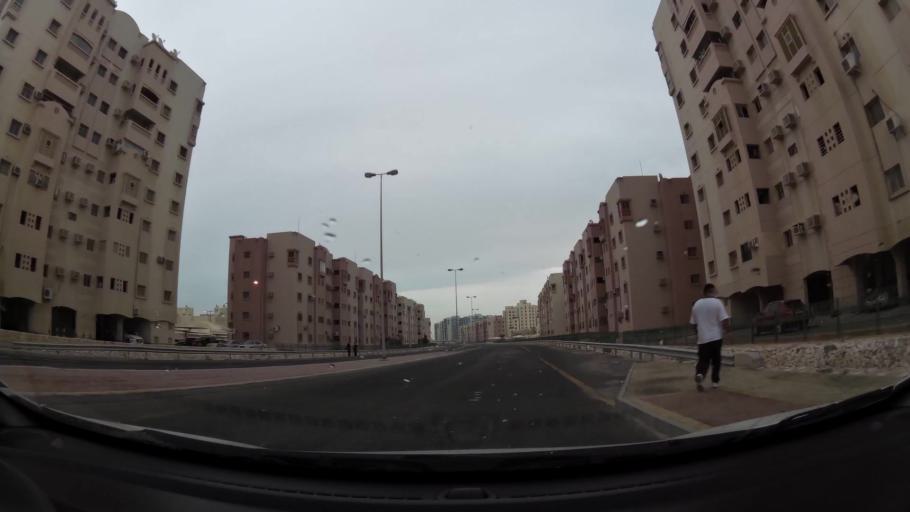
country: BH
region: Central Governorate
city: Madinat Hamad
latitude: 26.1201
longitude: 50.4875
